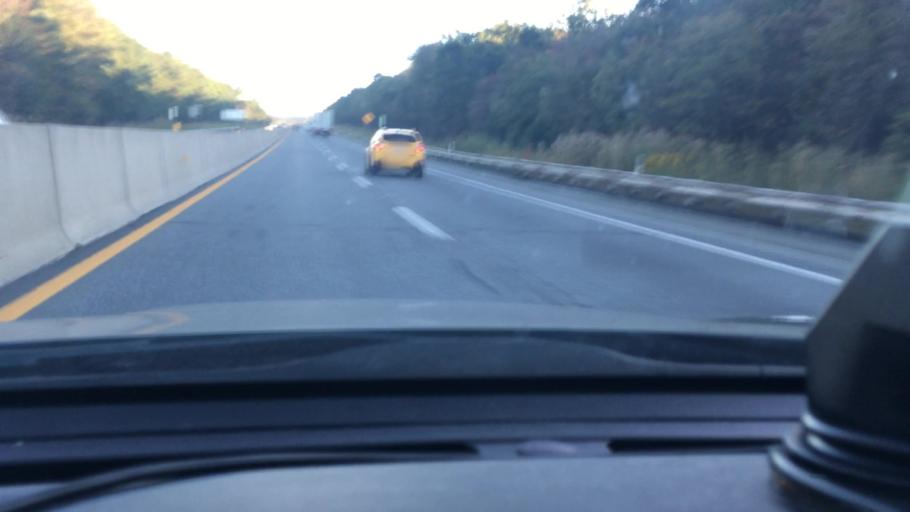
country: US
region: Pennsylvania
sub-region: Carbon County
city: Towamensing Trails
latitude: 40.9558
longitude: -75.6332
